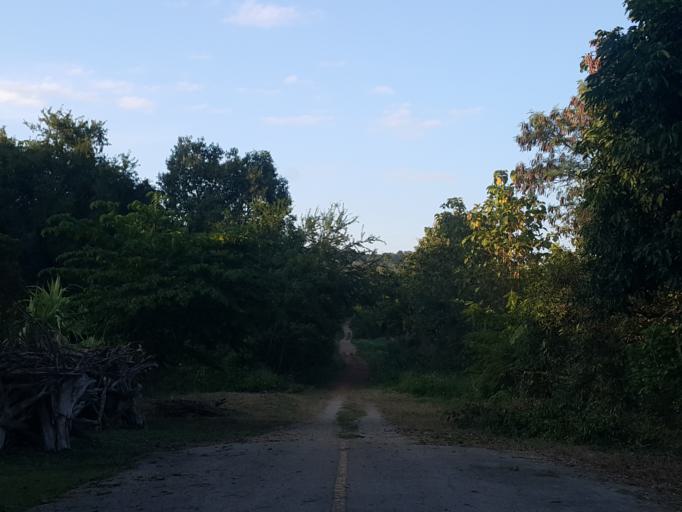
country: TH
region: Lampang
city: Lampang
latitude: 18.4412
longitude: 99.5718
